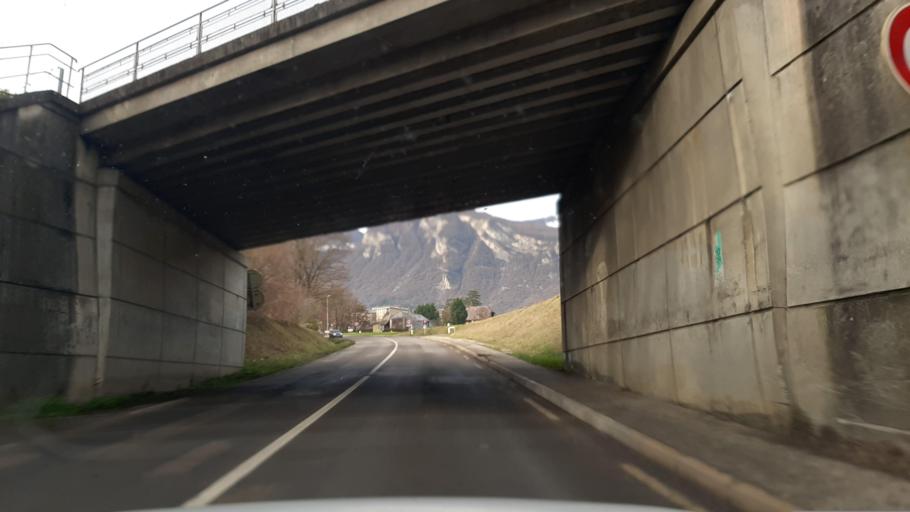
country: FR
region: Rhone-Alpes
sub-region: Departement de la Savoie
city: Coise-Saint-Jean-Pied-Gauthier
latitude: 45.5583
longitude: 6.1624
